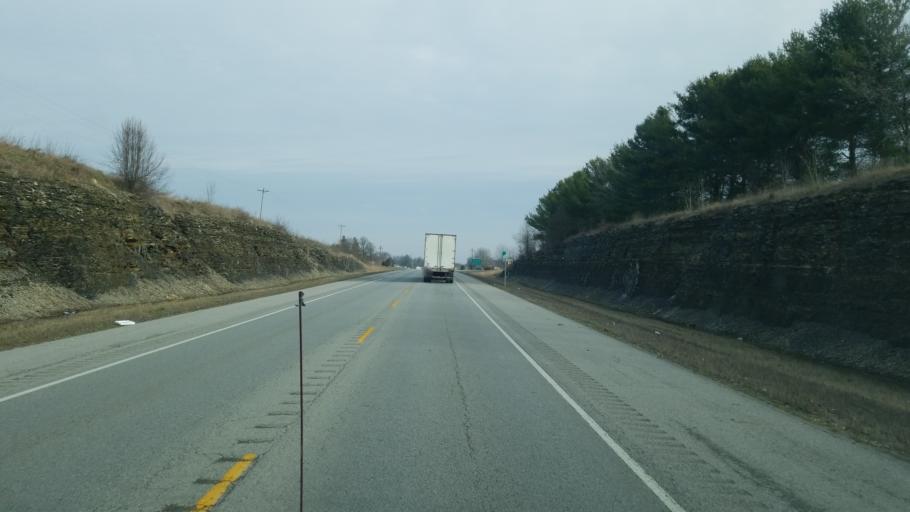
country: US
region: Kentucky
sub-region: Boyle County
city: Junction City
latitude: 37.5724
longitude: -84.7939
